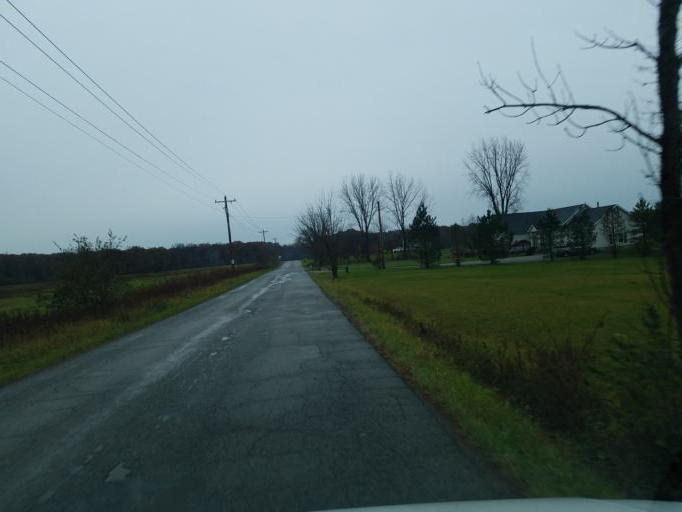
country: US
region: Ohio
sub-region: Delaware County
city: Ashley
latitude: 40.3607
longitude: -82.9254
